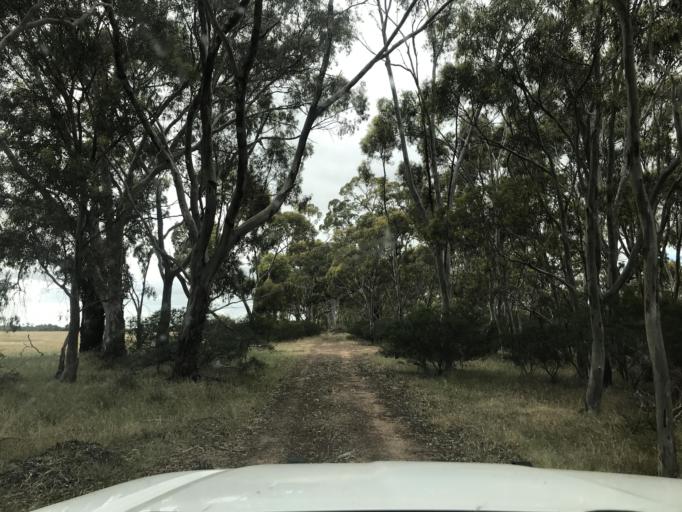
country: AU
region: South Australia
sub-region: Naracoorte and Lucindale
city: Naracoorte
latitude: -36.9024
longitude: 141.4201
